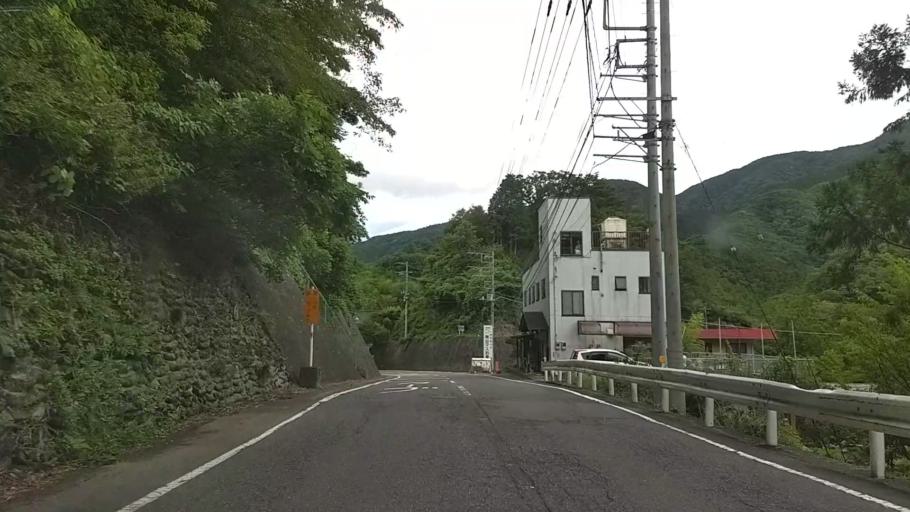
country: JP
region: Yamanashi
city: Uenohara
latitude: 35.5707
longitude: 139.0743
